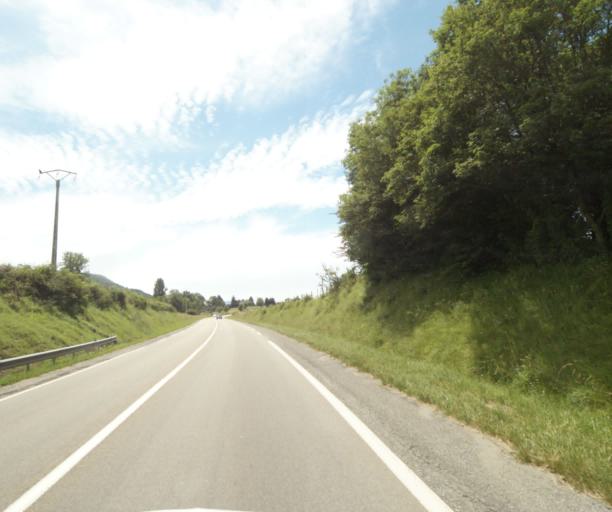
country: FR
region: Rhone-Alpes
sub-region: Departement de la Haute-Savoie
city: Allinges
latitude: 46.3392
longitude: 6.4579
